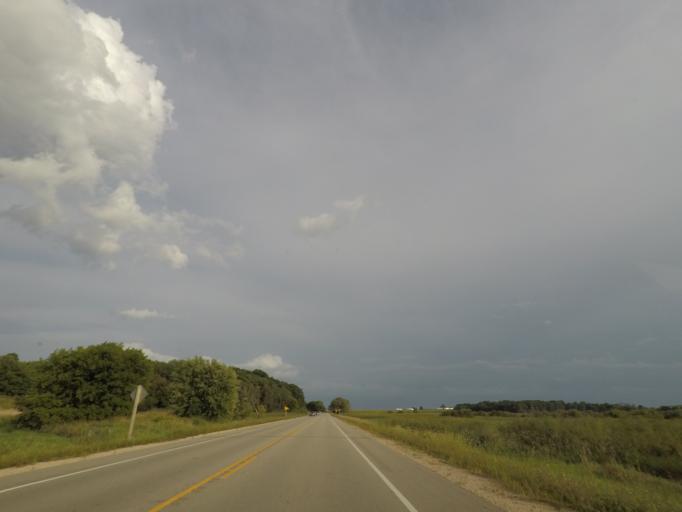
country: US
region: Wisconsin
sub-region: Dane County
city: Waunakee
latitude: 43.1903
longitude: -89.5093
